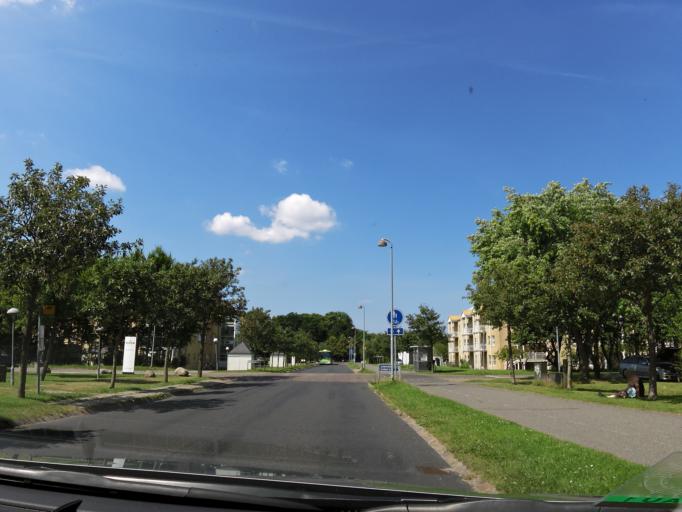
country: DK
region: South Denmark
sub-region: Odense Kommune
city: Neder Holluf
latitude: 55.3796
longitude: 10.4487
